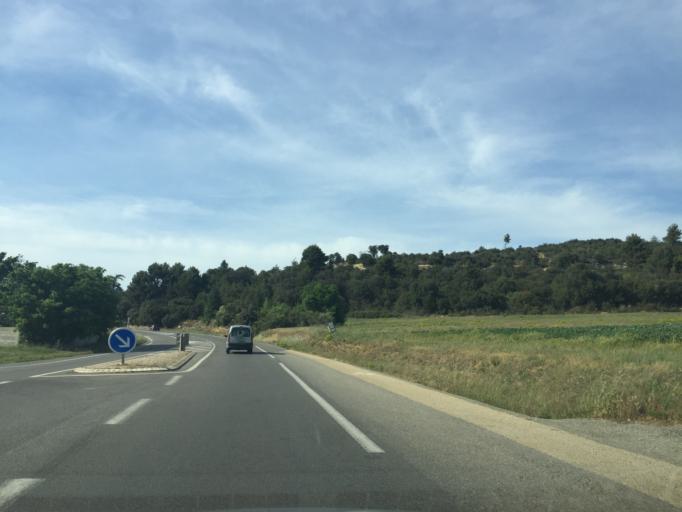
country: FR
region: Provence-Alpes-Cote d'Azur
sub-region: Departement du Var
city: Vinon-sur-Verdon
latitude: 43.7361
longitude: 5.8041
